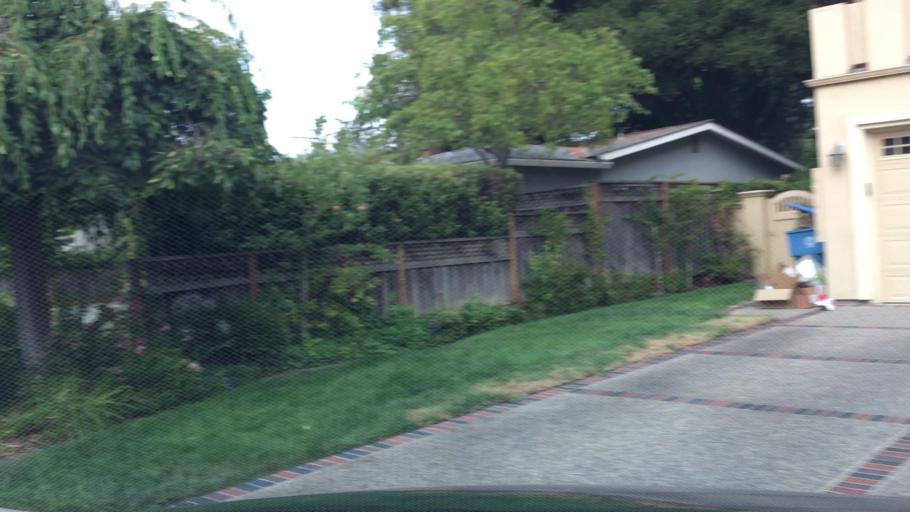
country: US
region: California
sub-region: Santa Clara County
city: Los Altos
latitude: 37.4110
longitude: -122.1273
